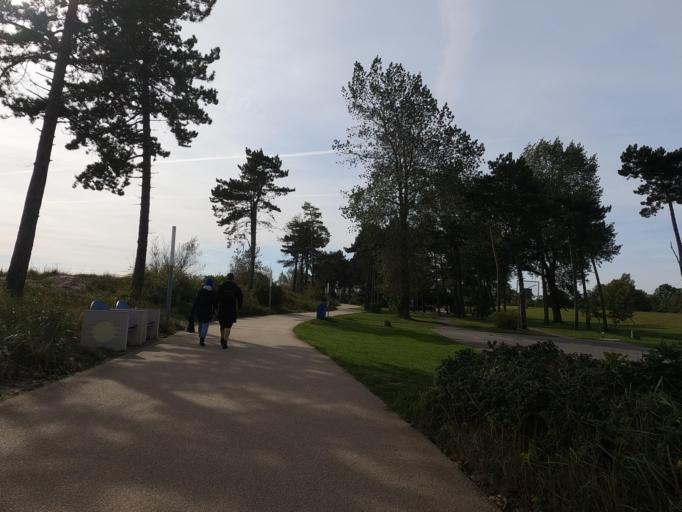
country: DE
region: Schleswig-Holstein
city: Kellenhusen
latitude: 54.1843
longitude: 11.0580
